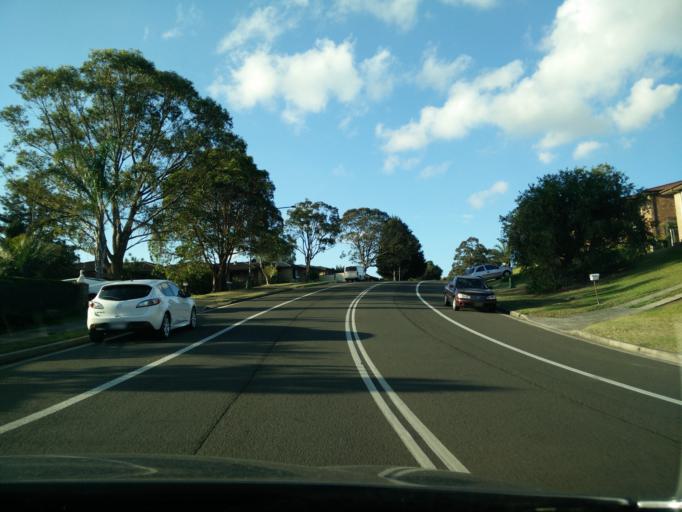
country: AU
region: New South Wales
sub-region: Wollongong
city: Berkeley
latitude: -34.4692
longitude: 150.8443
